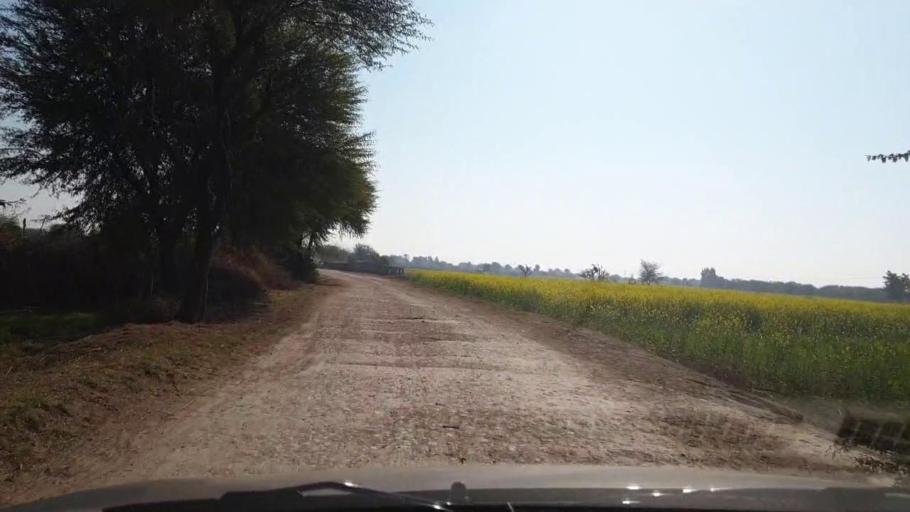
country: PK
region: Sindh
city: Jhol
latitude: 25.9347
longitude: 68.8239
